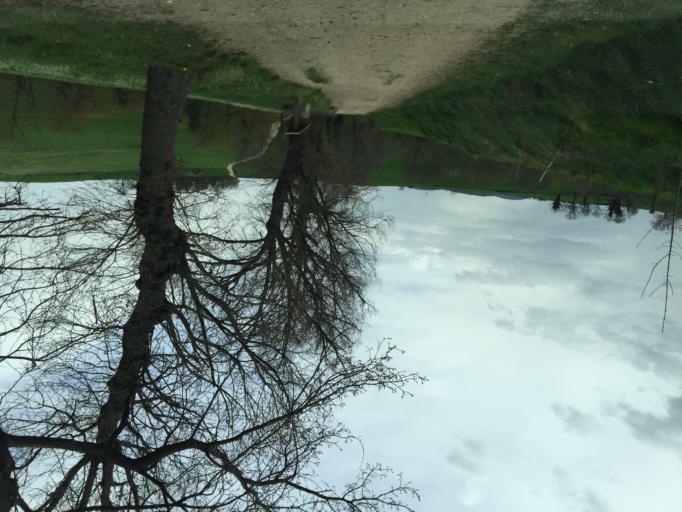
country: FR
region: Rhone-Alpes
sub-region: Departement de la Loire
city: Saint-Paul-en-Jarez
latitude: 45.4779
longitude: 4.5641
